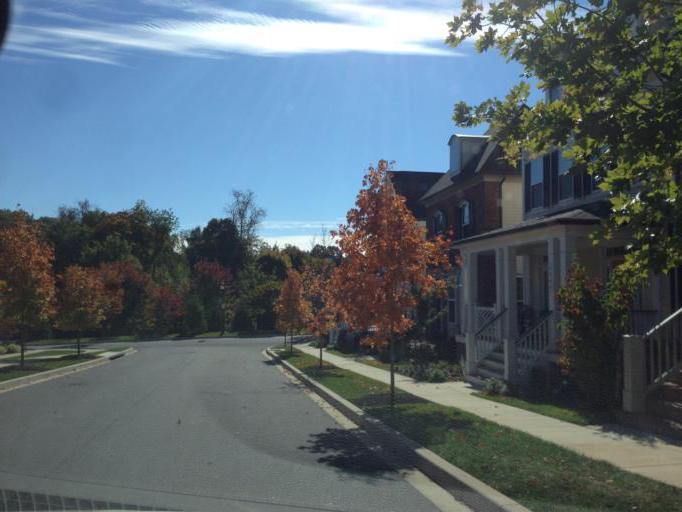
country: US
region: Maryland
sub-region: Howard County
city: Fulton
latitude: 39.1519
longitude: -76.8984
